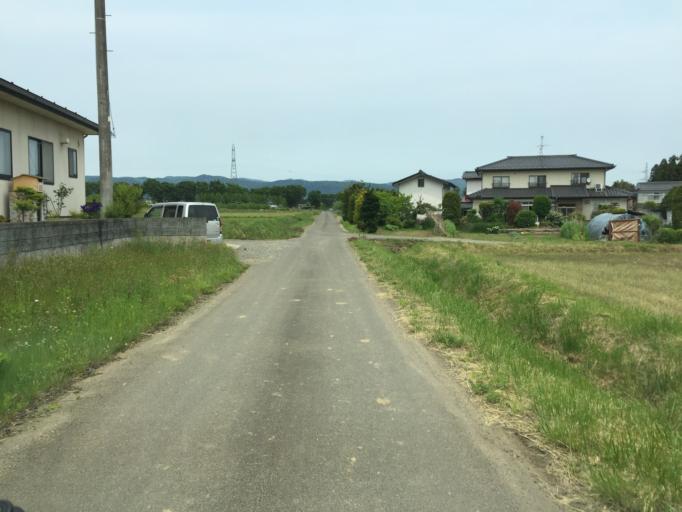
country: JP
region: Fukushima
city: Fukushima-shi
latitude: 37.7288
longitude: 140.4008
